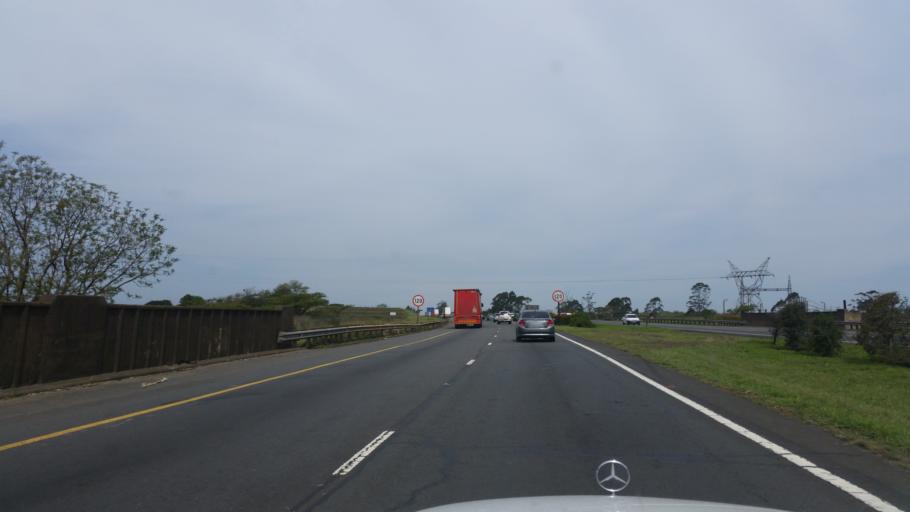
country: ZA
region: KwaZulu-Natal
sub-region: uMgungundlovu District Municipality
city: Camperdown
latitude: -29.7245
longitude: 30.5035
